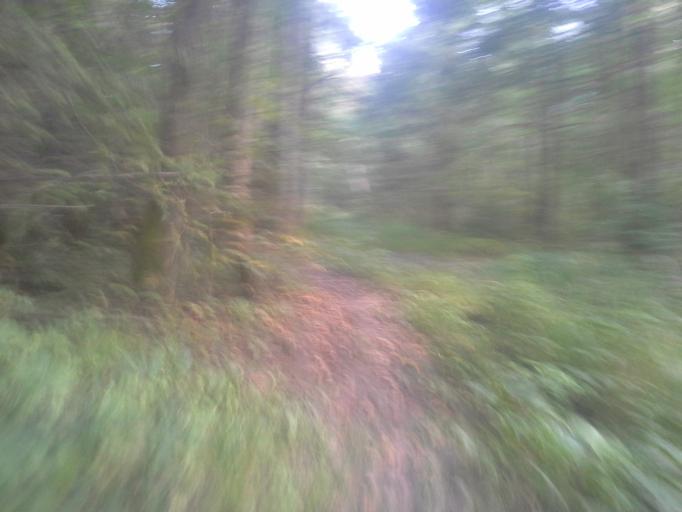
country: RU
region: Moskovskaya
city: Kievskij
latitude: 55.3648
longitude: 36.9042
